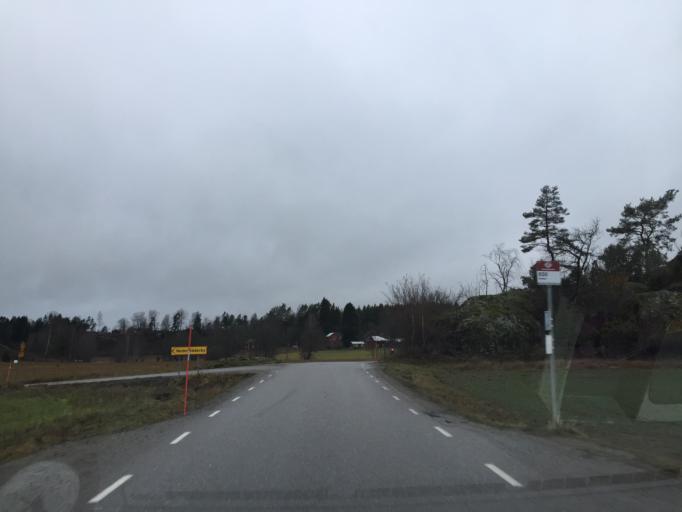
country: SE
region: Stockholm
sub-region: Nynashamns Kommun
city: Osmo
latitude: 59.0413
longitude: 17.8859
